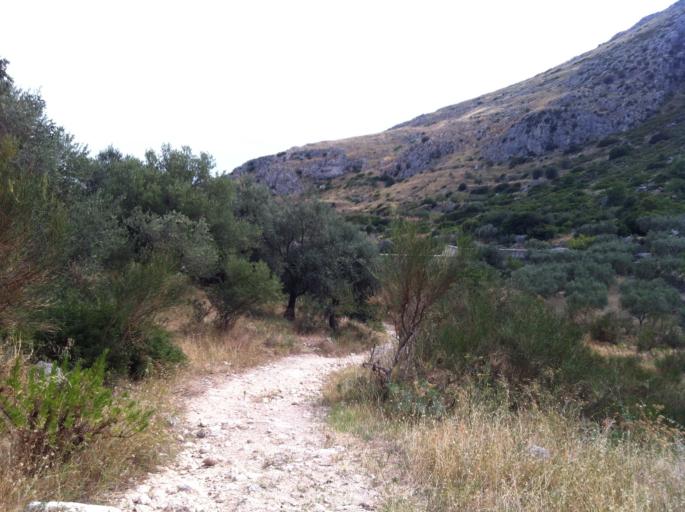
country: IT
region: Apulia
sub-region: Provincia di Foggia
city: Manfredonia
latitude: 41.6698
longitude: 15.9091
